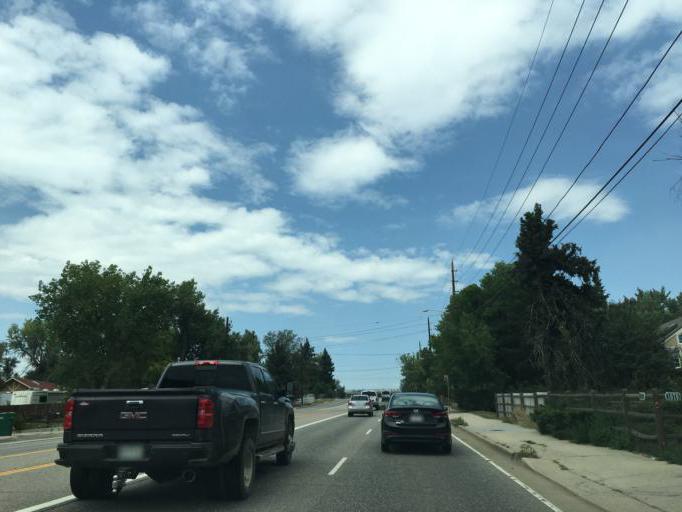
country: US
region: Colorado
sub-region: Jefferson County
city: Lakewood
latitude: 39.7333
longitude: -105.1095
